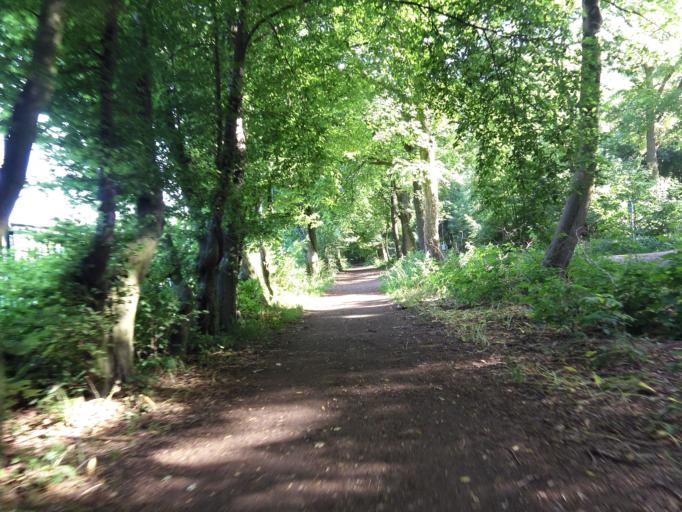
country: DE
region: Saxony
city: Leipzig
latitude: 51.3250
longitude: 12.3475
